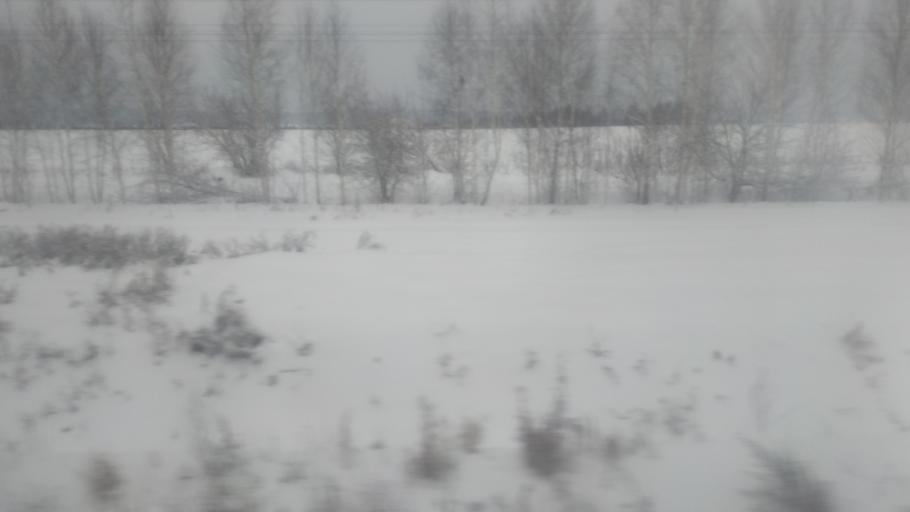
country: RU
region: Bashkortostan
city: Amzya
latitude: 56.2482
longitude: 54.6465
